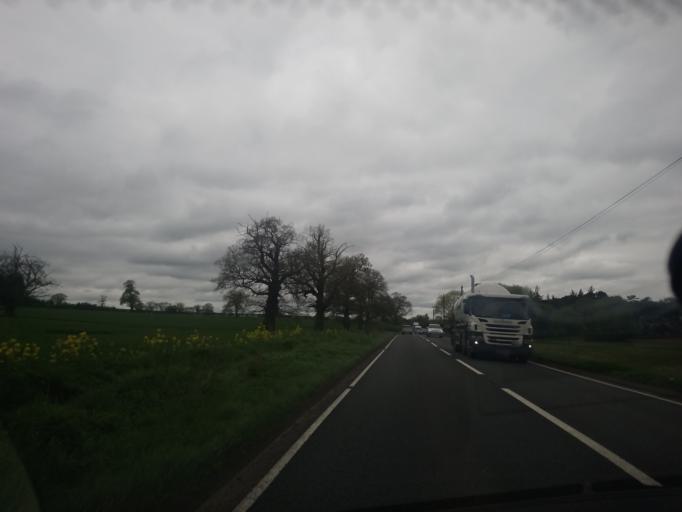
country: GB
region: England
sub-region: Telford and Wrekin
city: Chetwynd
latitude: 52.8019
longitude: -2.4271
